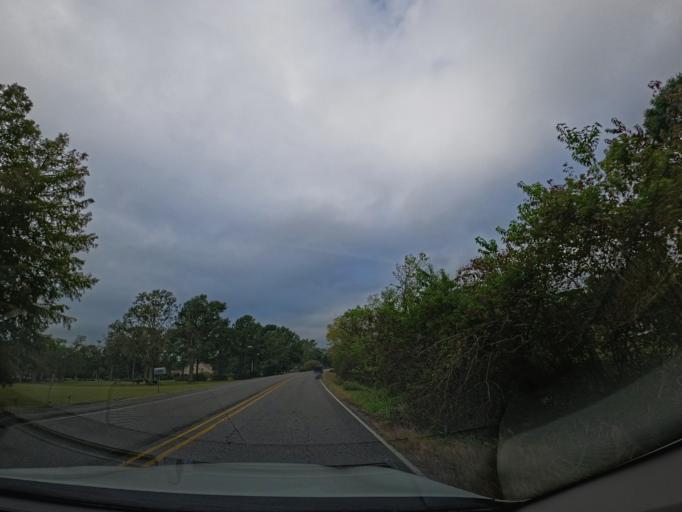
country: US
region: Louisiana
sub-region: Terrebonne Parish
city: Houma
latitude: 29.5736
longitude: -90.7519
